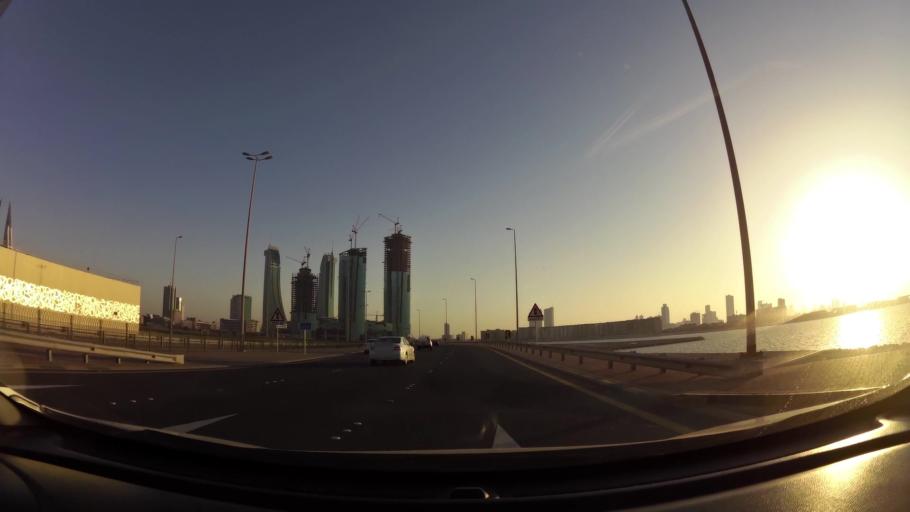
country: BH
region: Manama
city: Manama
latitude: 26.2480
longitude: 50.5753
